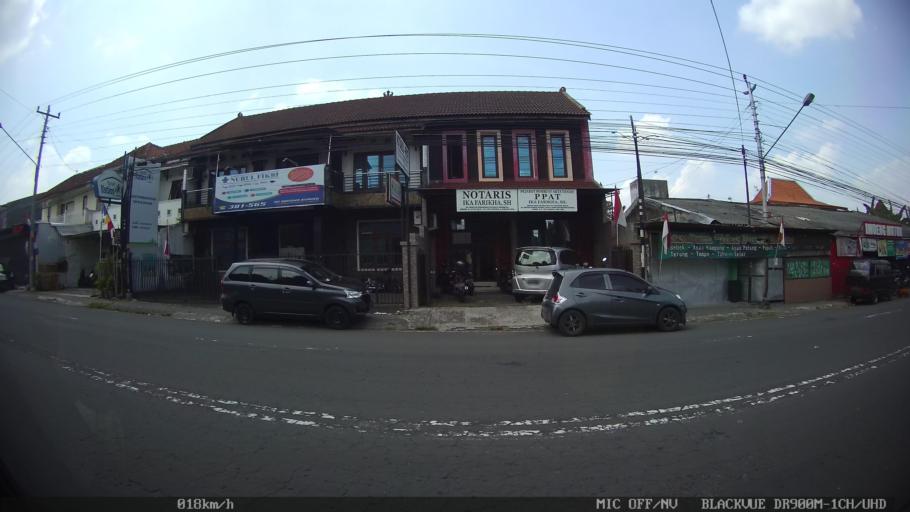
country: ID
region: Daerah Istimewa Yogyakarta
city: Yogyakarta
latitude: -7.8116
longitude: 110.4022
